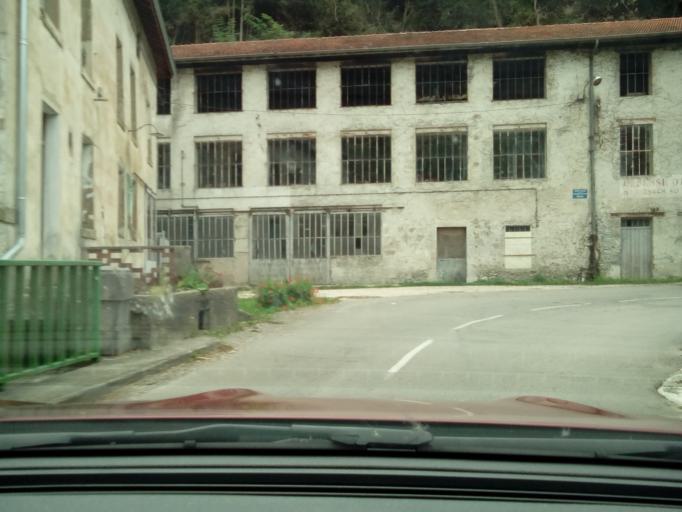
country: FR
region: Rhone-Alpes
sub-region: Departement de l'Isere
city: Pont-en-Royans
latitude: 45.0555
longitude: 5.3432
